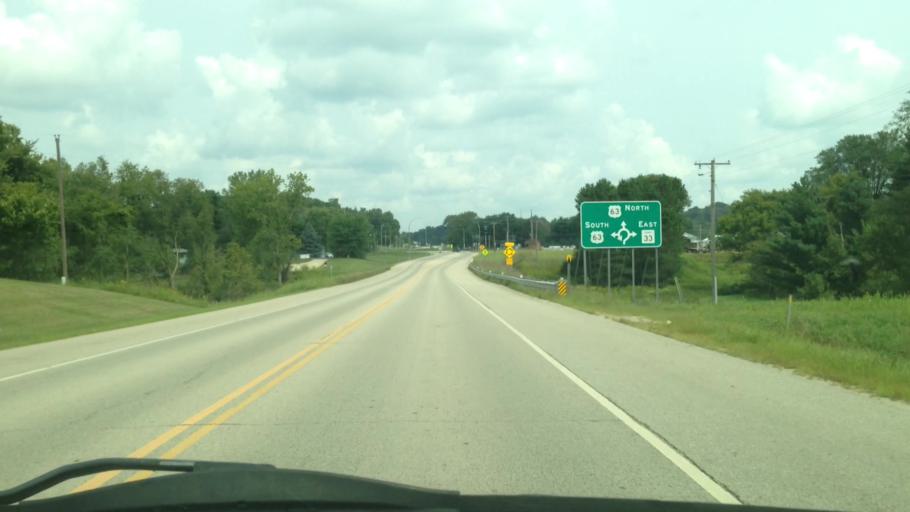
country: US
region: Minnesota
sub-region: Olmsted County
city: Rochester
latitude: 44.1045
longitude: -92.4336
